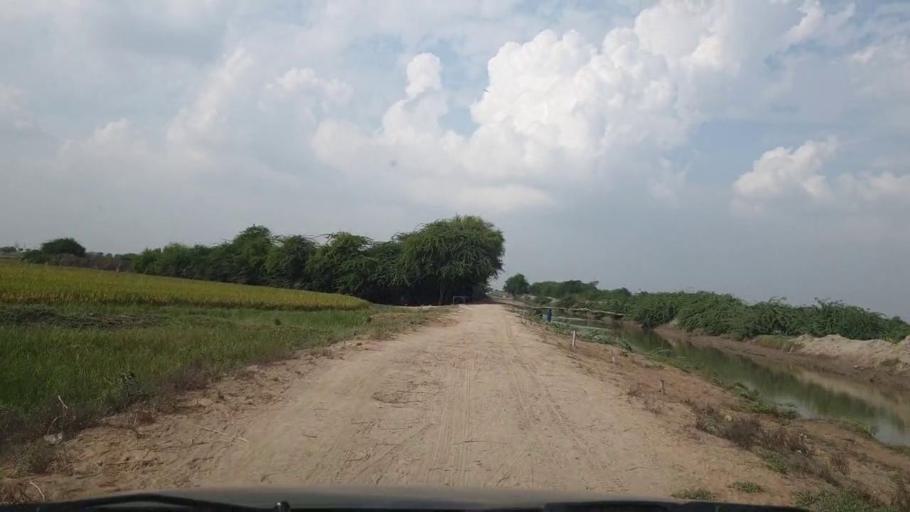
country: PK
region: Sindh
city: Badin
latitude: 24.5645
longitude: 68.6372
